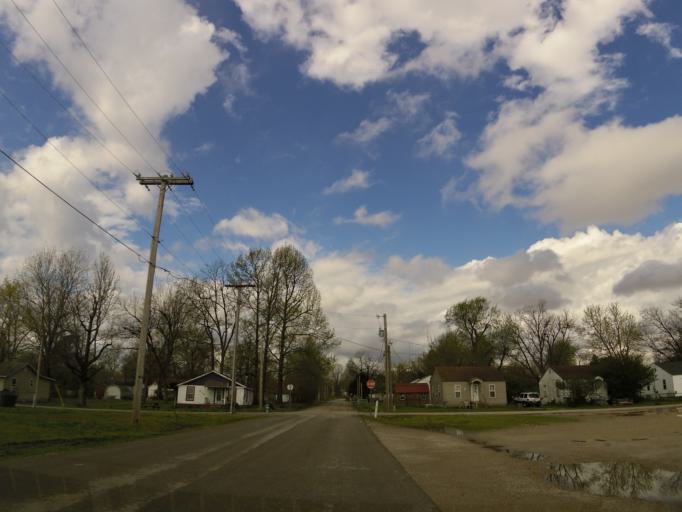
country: US
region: Missouri
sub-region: Butler County
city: Poplar Bluff
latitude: 36.7596
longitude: -90.3835
